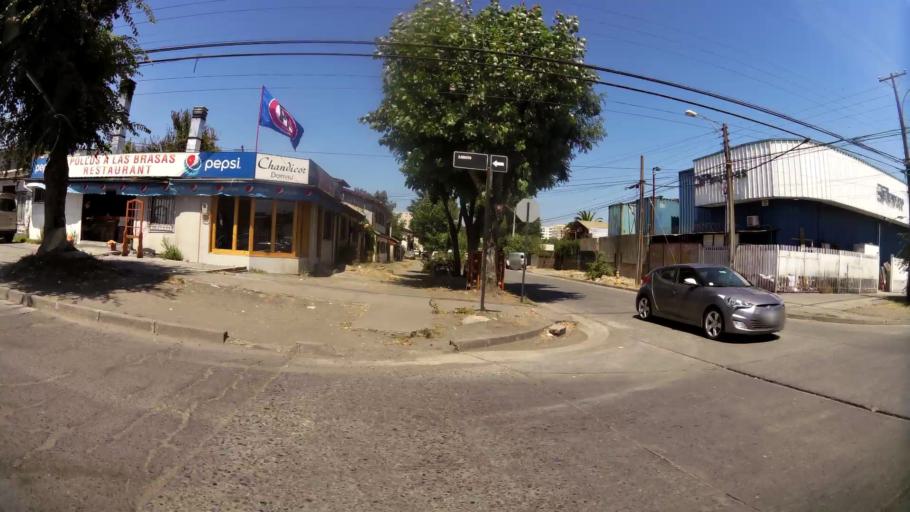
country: CL
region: Biobio
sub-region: Provincia de Concepcion
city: Concepcion
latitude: -36.8087
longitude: -73.0483
